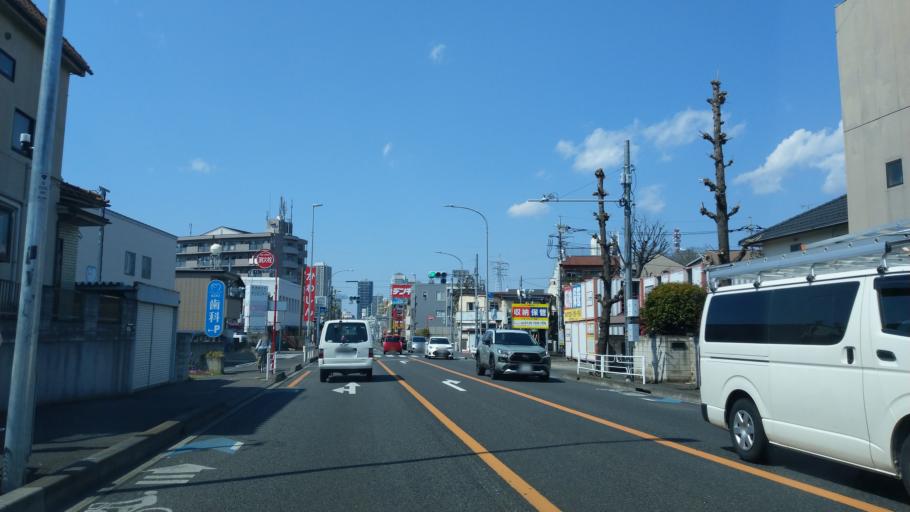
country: JP
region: Saitama
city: Yono
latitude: 35.8800
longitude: 139.6341
